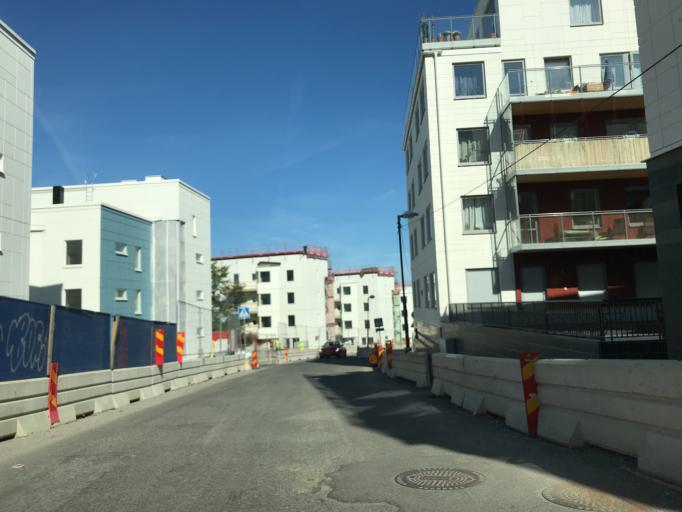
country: SE
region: Stockholm
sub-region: Stockholms Kommun
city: Arsta
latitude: 59.3093
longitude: 18.0167
